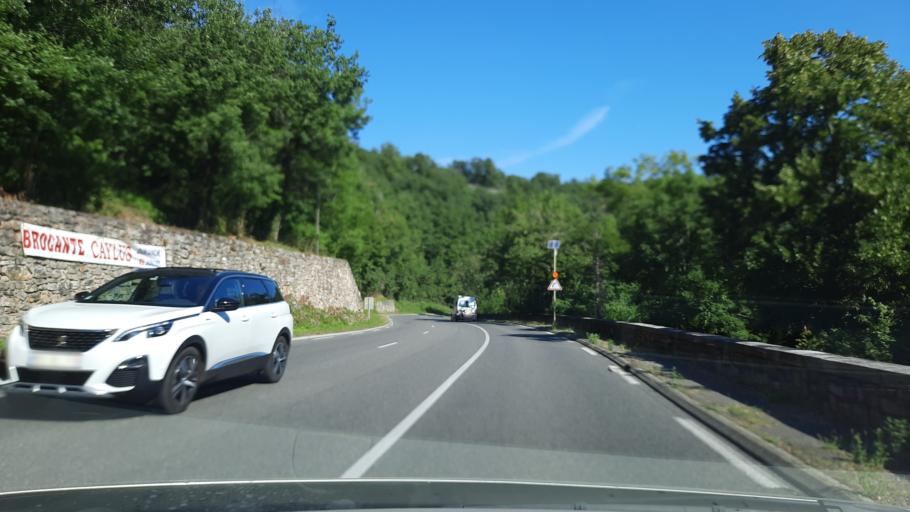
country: FR
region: Midi-Pyrenees
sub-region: Departement du Tarn-et-Garonne
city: Caylus
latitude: 44.2346
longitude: 1.7660
